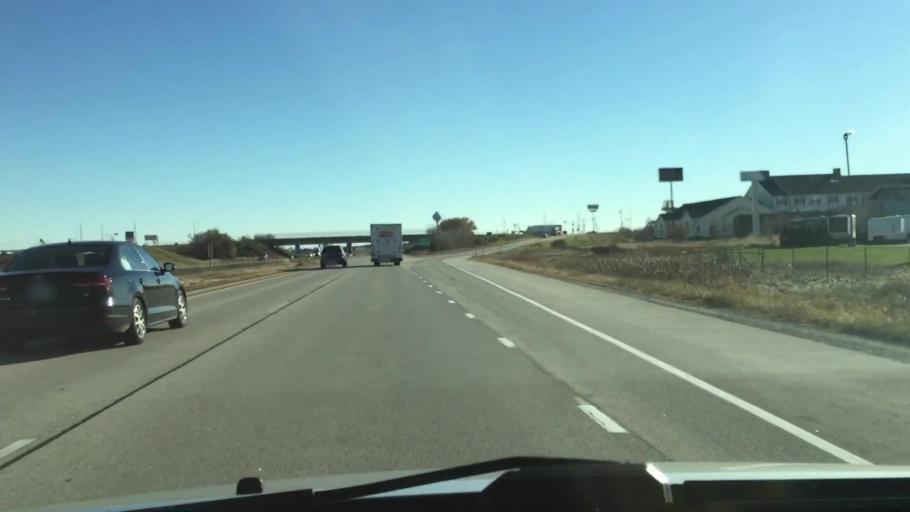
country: US
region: Wisconsin
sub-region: Outagamie County
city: Little Chute
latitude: 44.2977
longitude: -88.3176
